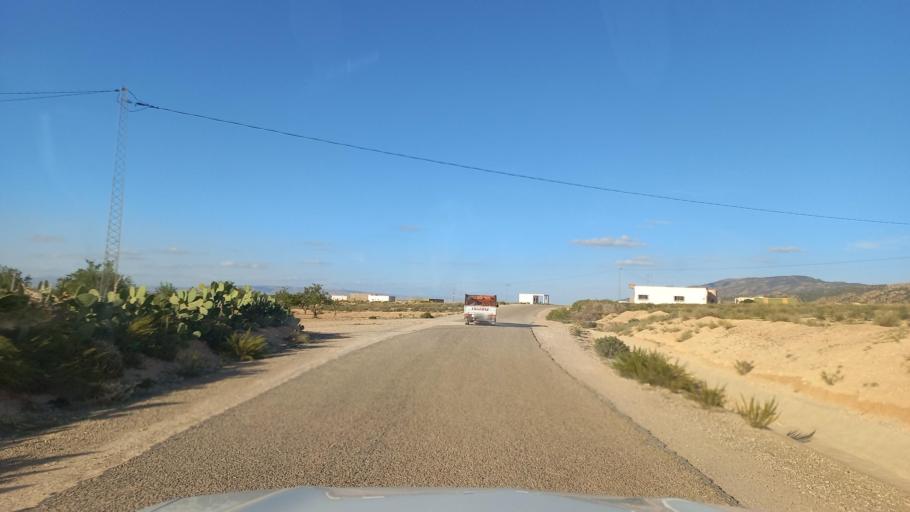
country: TN
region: Al Qasrayn
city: Sbiba
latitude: 35.3551
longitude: 9.1371
